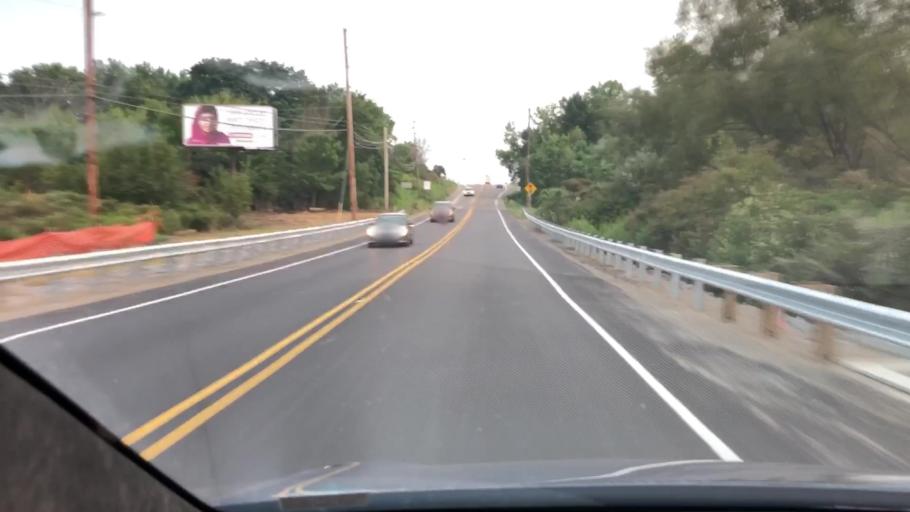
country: US
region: Pennsylvania
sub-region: Mercer County
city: Grove City
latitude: 41.2074
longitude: -79.9743
